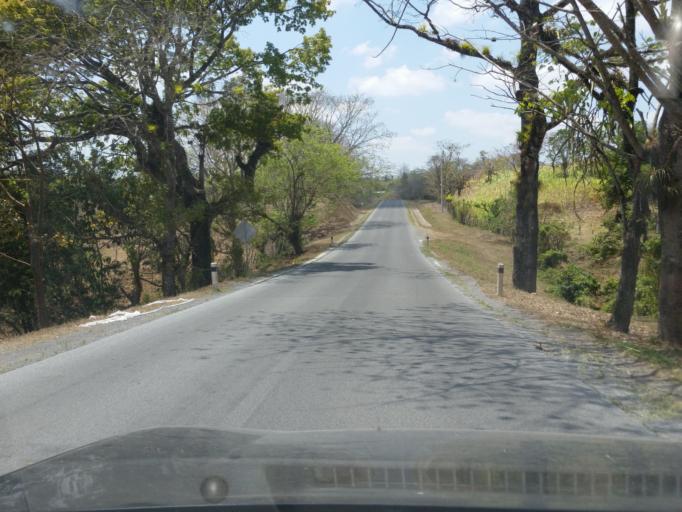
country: NI
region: Matagalpa
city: Muy Muy
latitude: 12.6139
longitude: -85.5351
